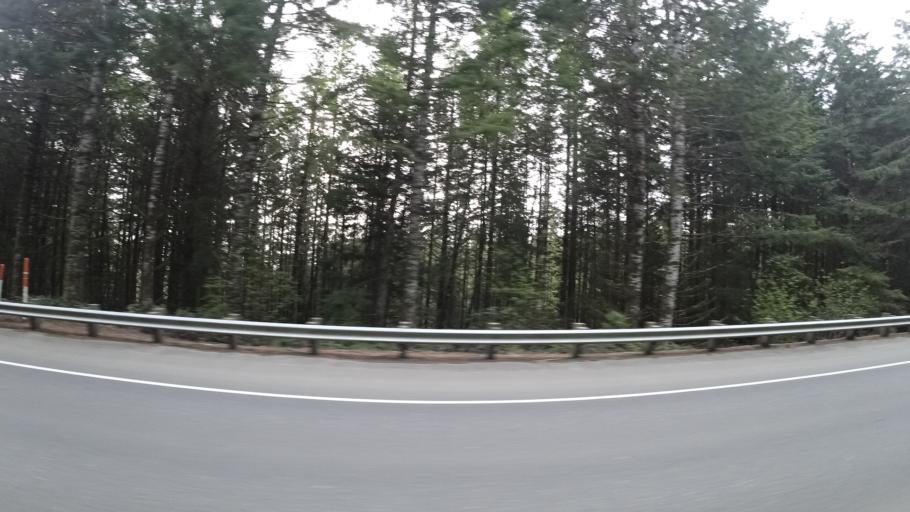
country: US
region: Oregon
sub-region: Coos County
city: Barview
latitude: 43.2484
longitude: -124.2869
